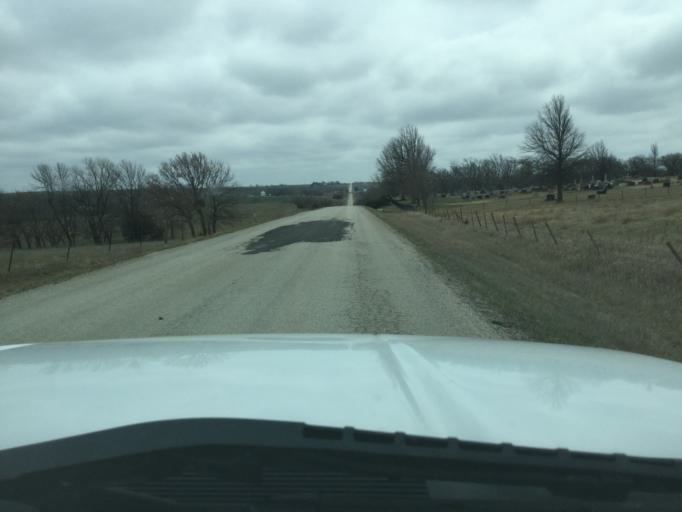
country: US
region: Kansas
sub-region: Nemaha County
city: Seneca
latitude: 39.7399
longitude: -95.9981
